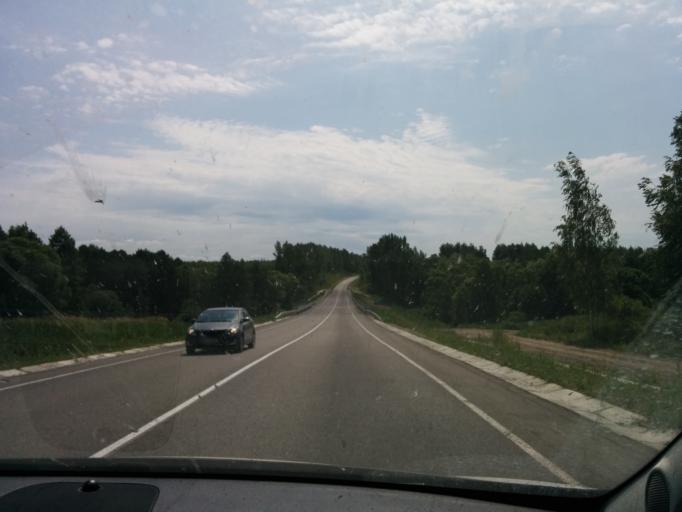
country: RU
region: Tambov
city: Morshansk
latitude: 53.5405
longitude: 41.7903
